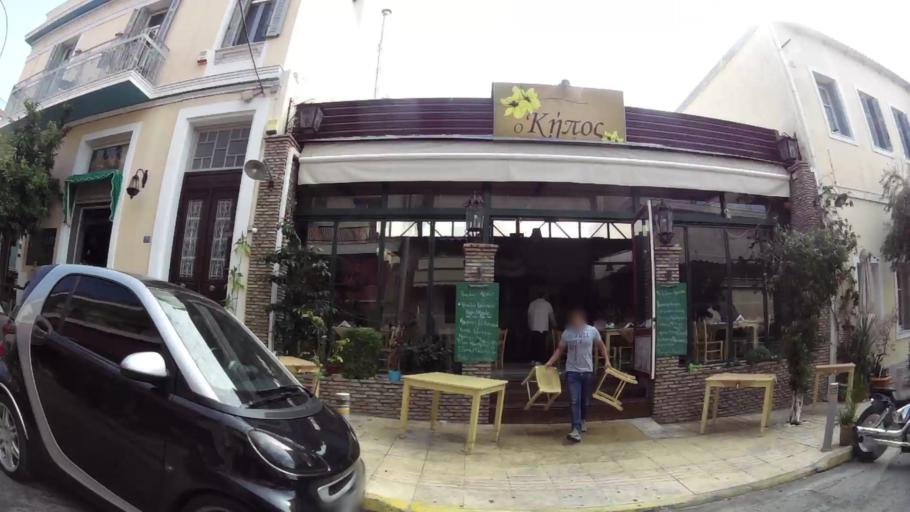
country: GR
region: Attica
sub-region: Nomarchia Athinas
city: Athens
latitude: 37.9699
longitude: 23.7133
